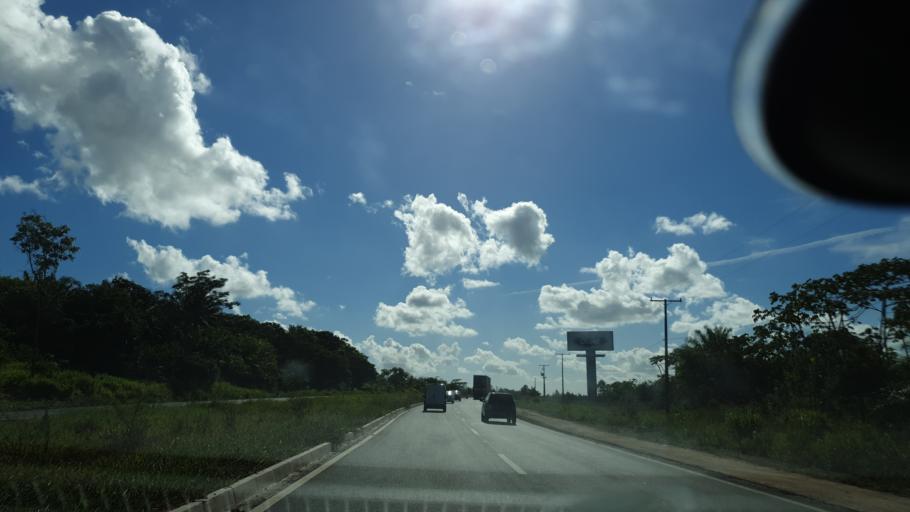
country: BR
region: Bahia
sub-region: Camacari
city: Camacari
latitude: -12.6815
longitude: -38.2878
